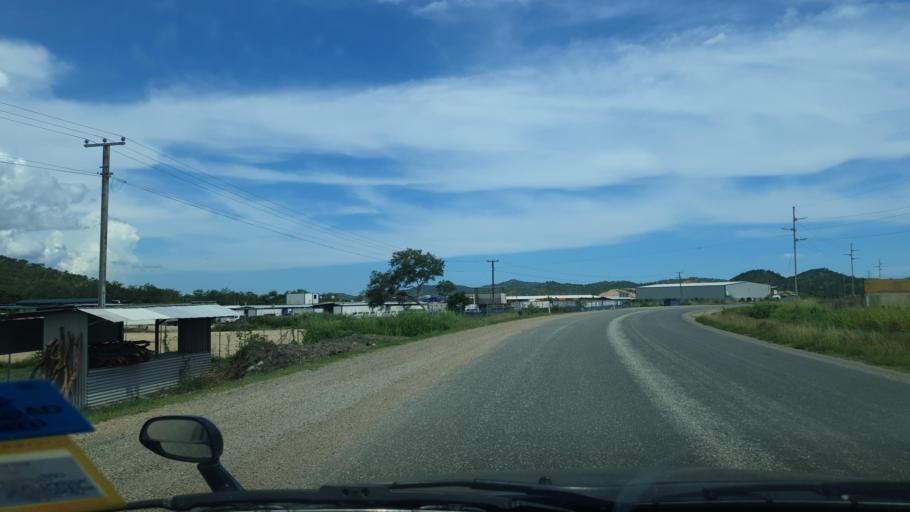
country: PG
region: National Capital
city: Port Moresby
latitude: -9.4102
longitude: 147.0721
